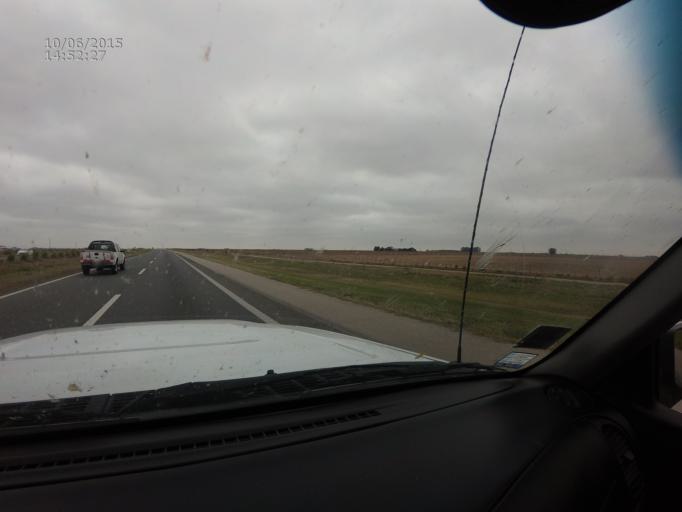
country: AR
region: Cordoba
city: Oncativo
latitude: -31.8827
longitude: -63.6579
